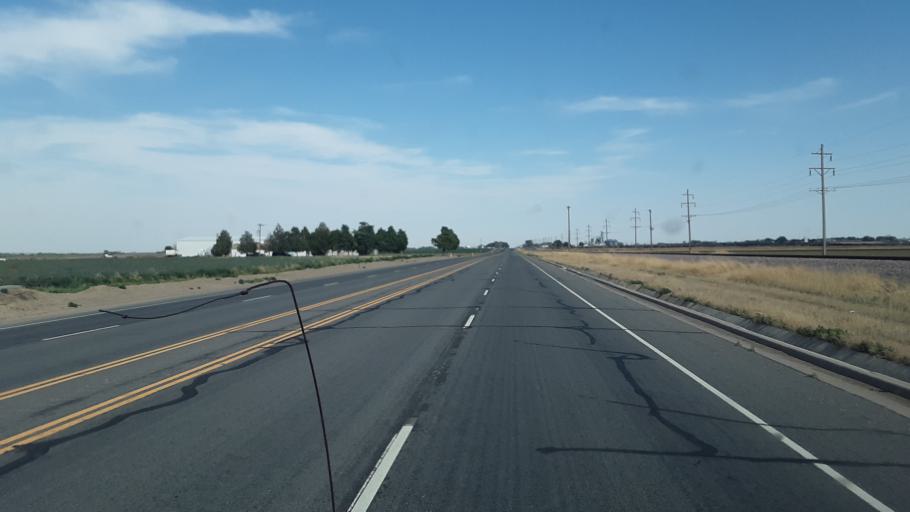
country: US
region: Colorado
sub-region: Otero County
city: Rocky Ford
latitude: 38.0857
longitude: -103.8011
